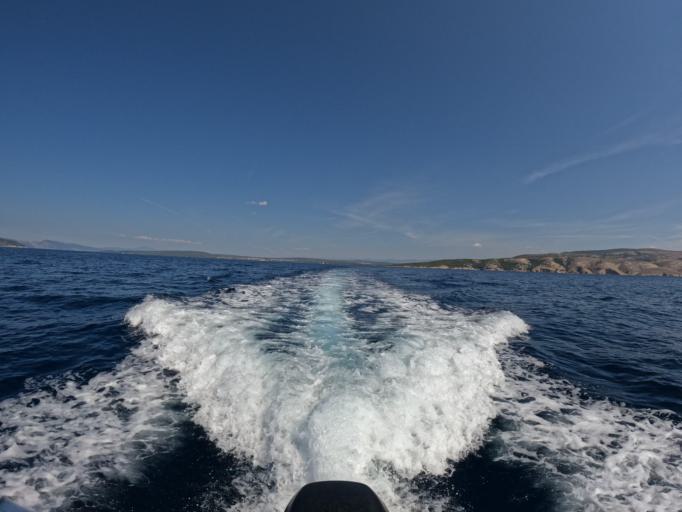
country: HR
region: Primorsko-Goranska
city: Punat
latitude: 44.9514
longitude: 14.6120
